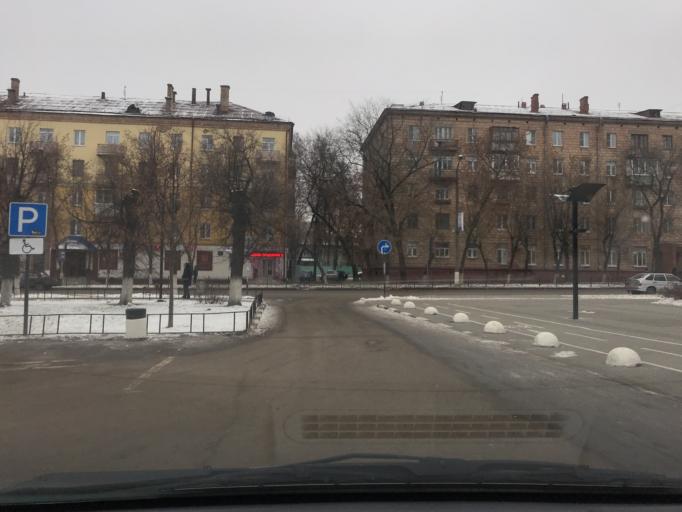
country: RU
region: Moskovskaya
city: Elektrostal'
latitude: 55.7847
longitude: 38.4465
